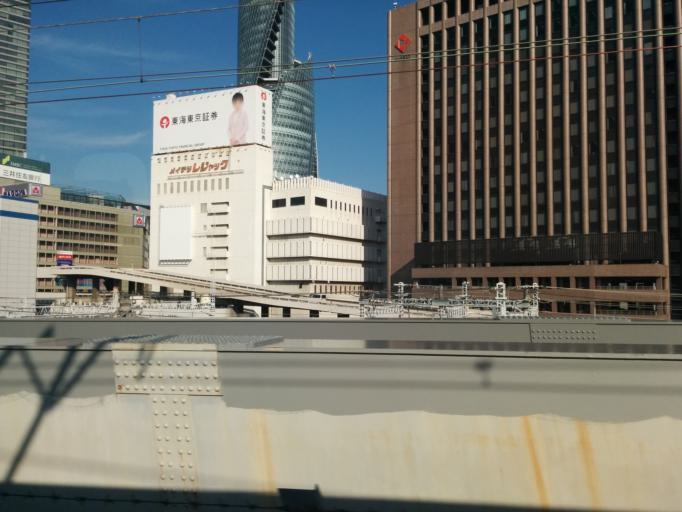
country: JP
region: Aichi
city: Nagoya-shi
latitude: 35.1662
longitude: 136.8838
